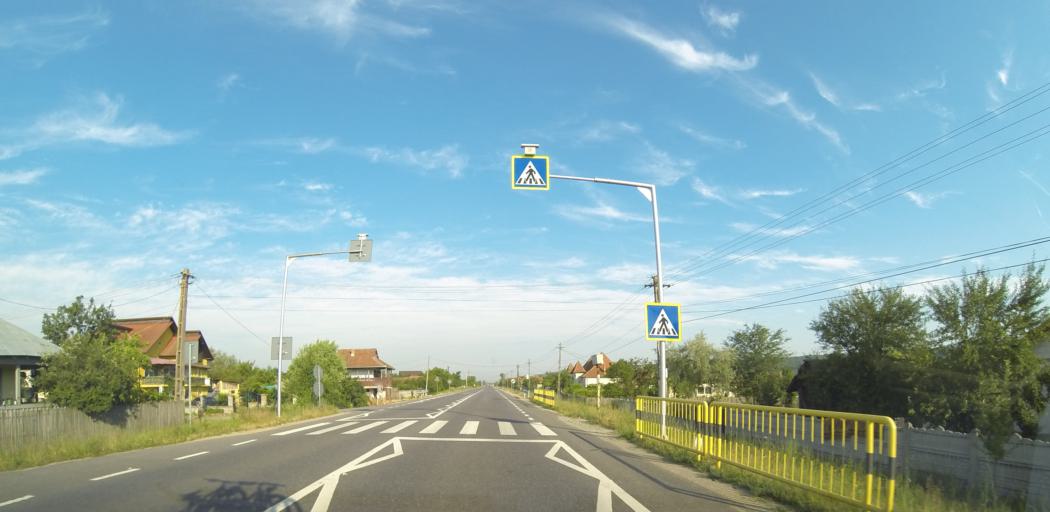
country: RO
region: Gorj
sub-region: Comuna Ionesti
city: Ionesti
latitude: 44.5750
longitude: 23.4150
